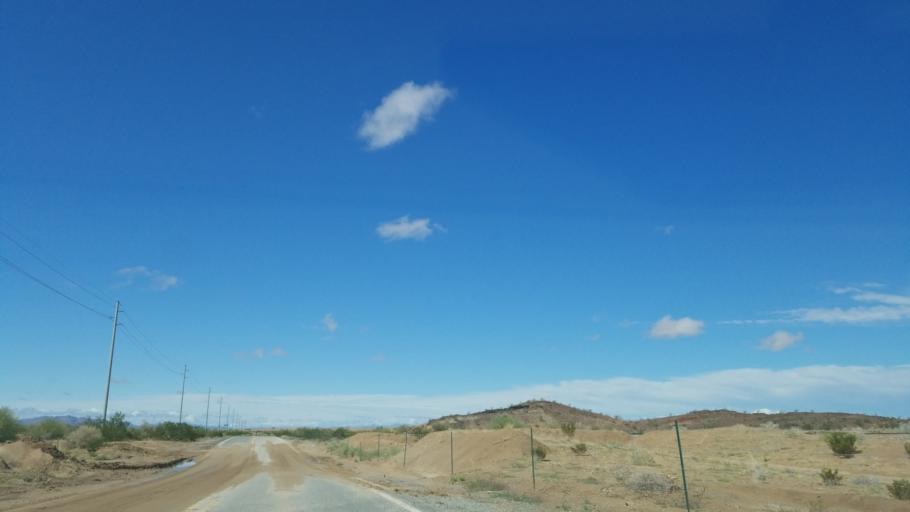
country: US
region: Arizona
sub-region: La Paz County
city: Cienega Springs
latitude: 33.9912
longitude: -114.0812
